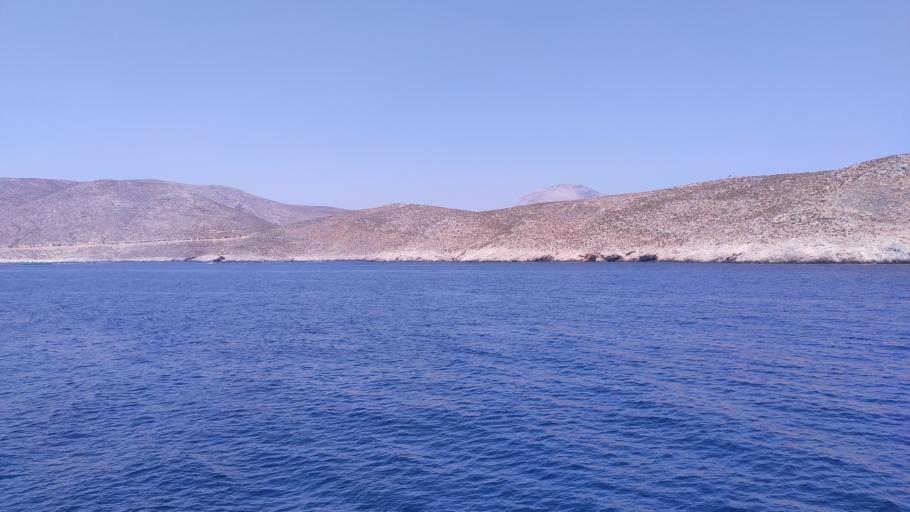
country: GR
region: South Aegean
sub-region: Nomos Dodekanisou
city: Kalymnos
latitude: 36.9413
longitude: 27.0475
